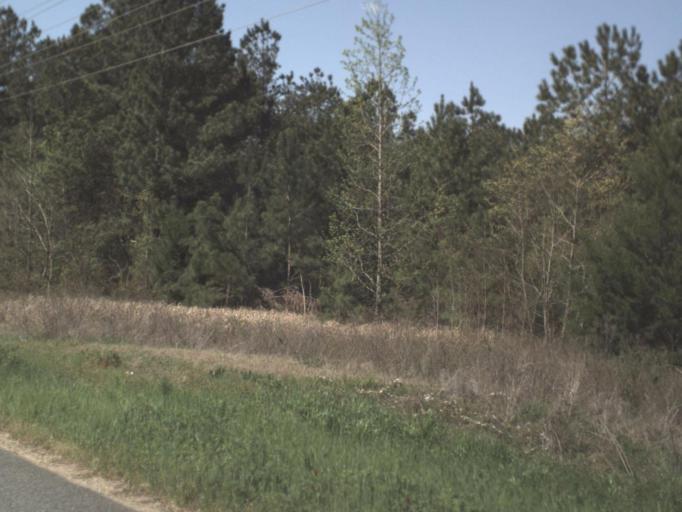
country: US
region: Florida
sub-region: Jackson County
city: Graceville
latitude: 30.9403
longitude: -85.4125
